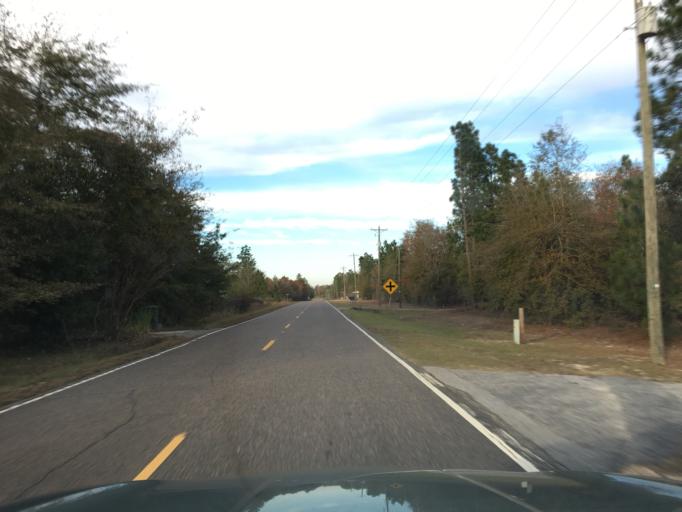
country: US
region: South Carolina
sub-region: Lexington County
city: Red Bank
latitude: 33.6980
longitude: -81.3596
